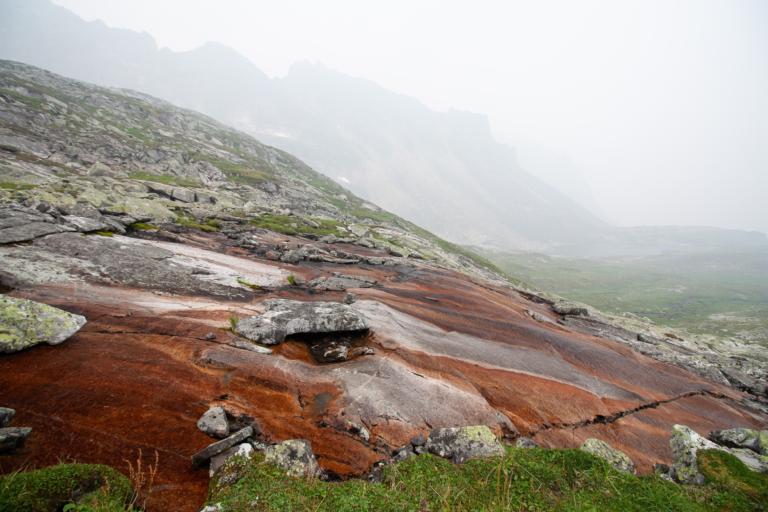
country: RU
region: Respublika Buryatiya
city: Kichera
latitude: 56.2372
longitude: 110.8620
